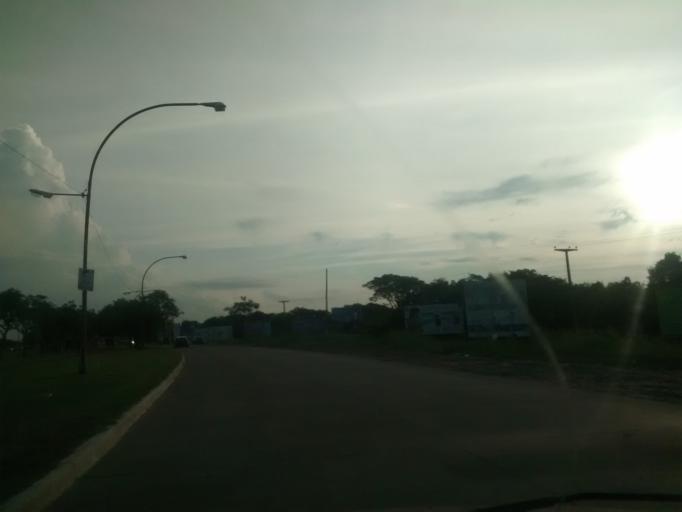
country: AR
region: Chaco
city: Resistencia
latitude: -27.4241
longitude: -58.9592
